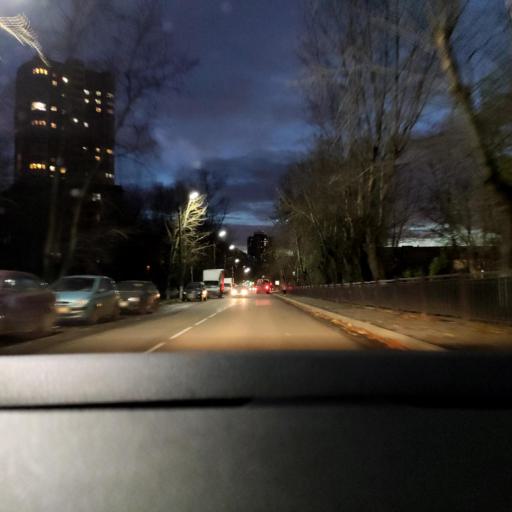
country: RU
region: Moskovskaya
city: Reutov
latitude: 55.7666
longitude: 37.8562
